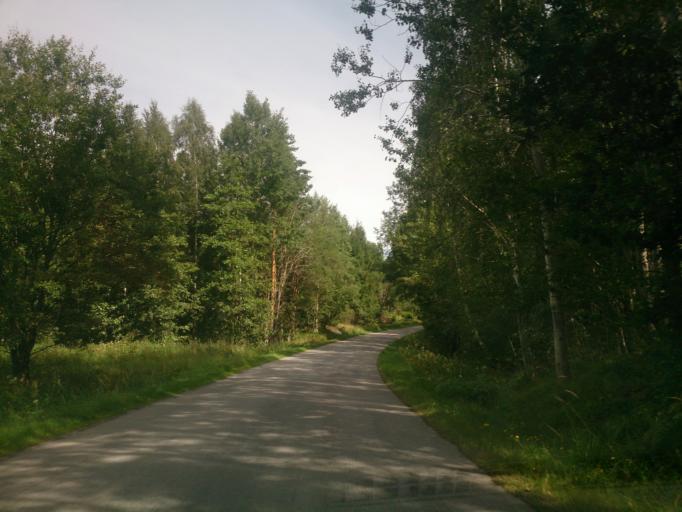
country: SE
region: OEstergoetland
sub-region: Valdemarsviks Kommun
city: Gusum
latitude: 58.3103
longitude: 16.5486
